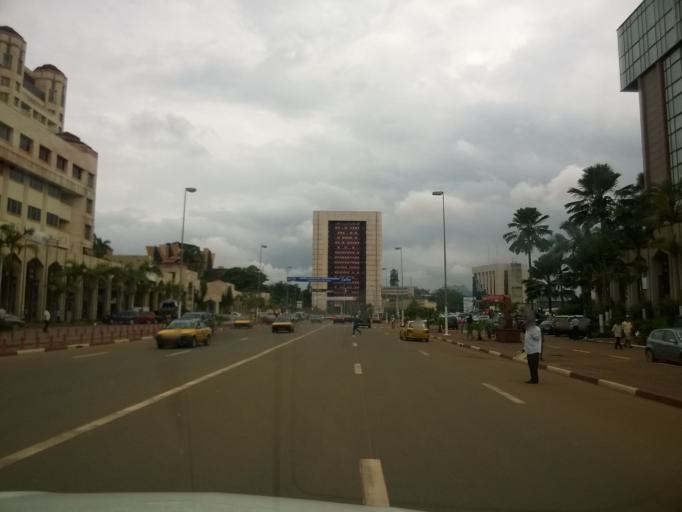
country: CM
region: Centre
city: Yaounde
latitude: 3.8643
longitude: 11.5173
